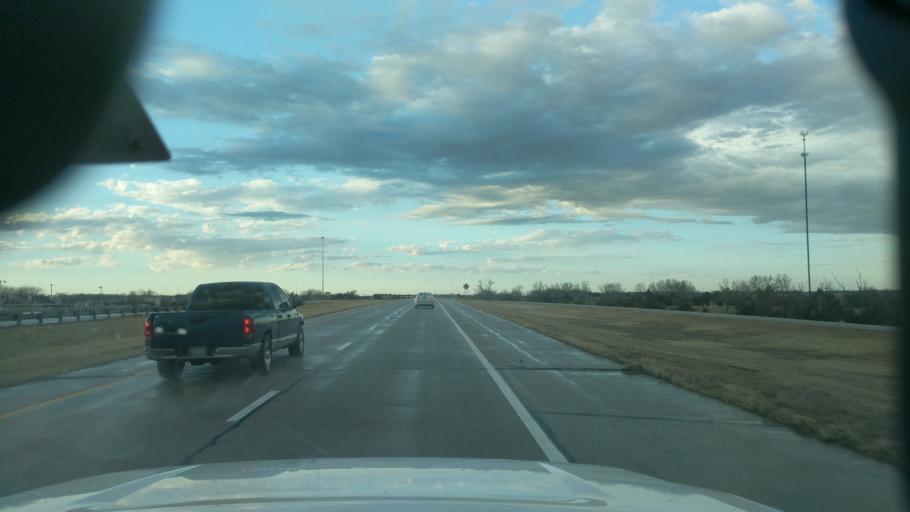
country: US
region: Kansas
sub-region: Harvey County
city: Hesston
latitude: 38.1449
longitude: -97.4174
